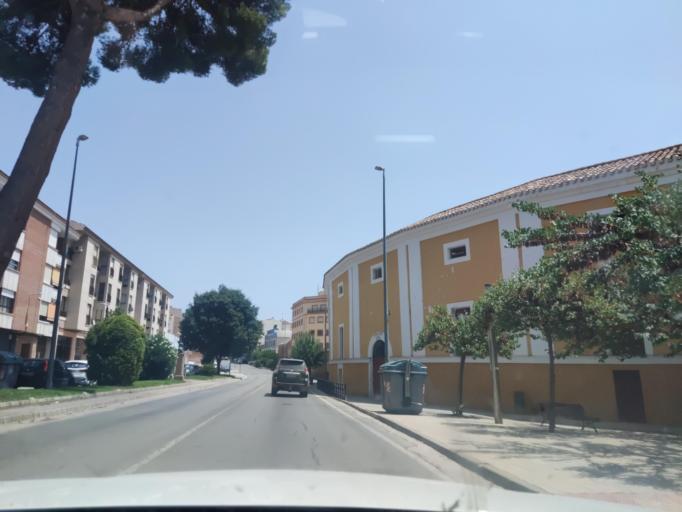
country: ES
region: Castille-La Mancha
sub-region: Provincia de Albacete
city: Hellin
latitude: 38.5111
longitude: -1.6963
